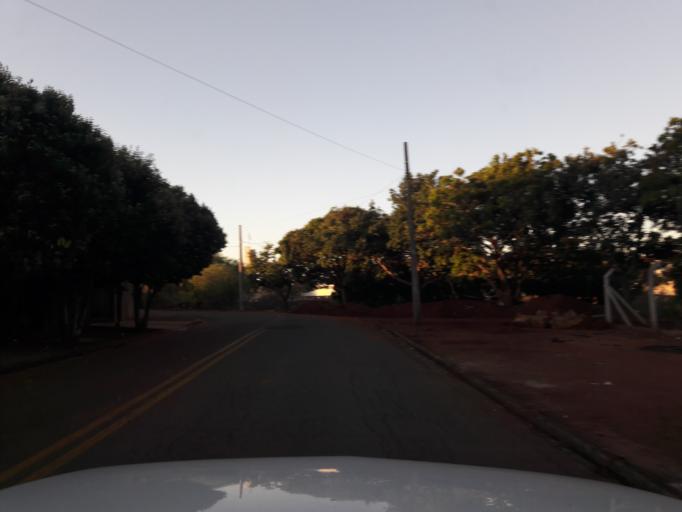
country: BR
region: Sao Paulo
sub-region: Moji-Guacu
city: Mogi-Gaucu
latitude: -22.3492
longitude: -46.9339
